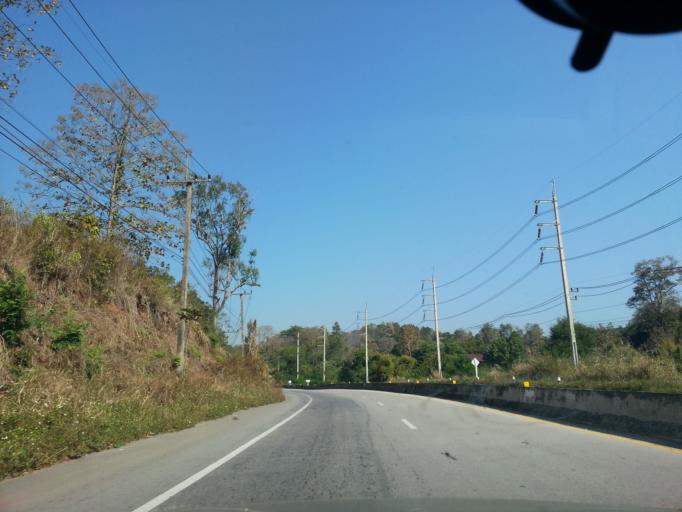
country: TH
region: Chiang Mai
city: Mae Taeng
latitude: 19.2320
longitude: 98.9684
